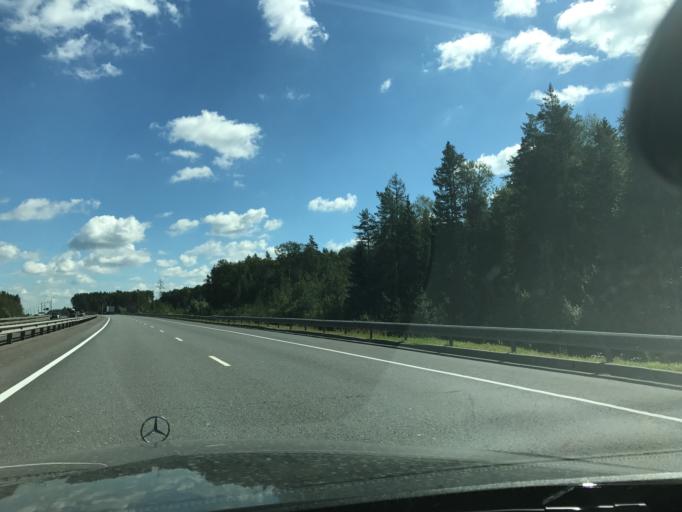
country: RU
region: Vladimir
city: Orgtrud
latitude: 56.1023
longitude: 40.7658
